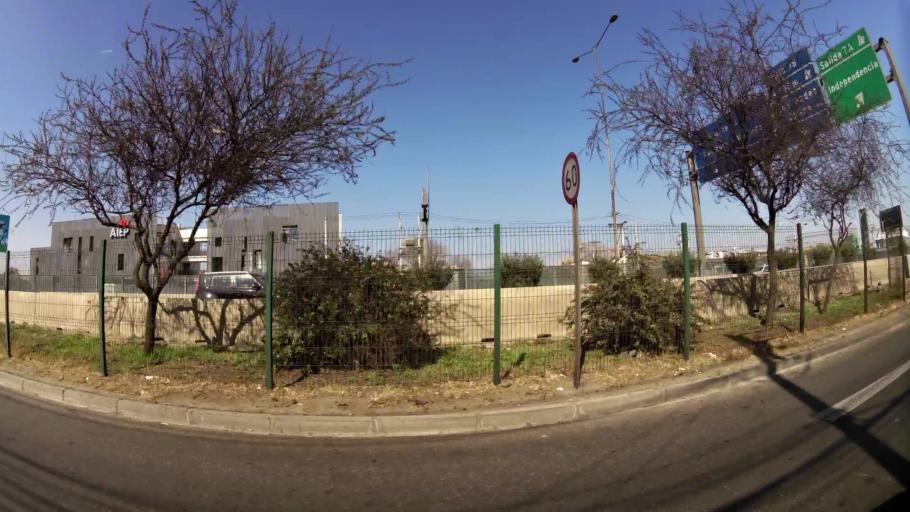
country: CL
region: Santiago Metropolitan
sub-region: Provincia de Chacabuco
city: Chicureo Abajo
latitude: -33.3672
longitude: -70.6809
